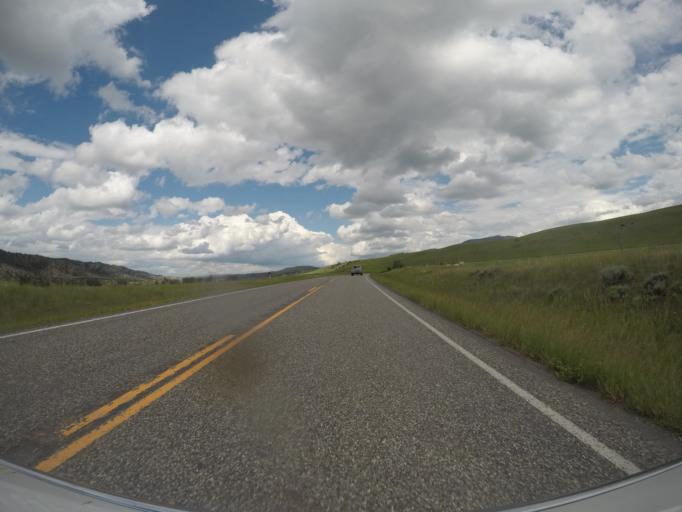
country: US
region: Montana
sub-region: Sweet Grass County
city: Big Timber
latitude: 45.6900
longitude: -110.0550
